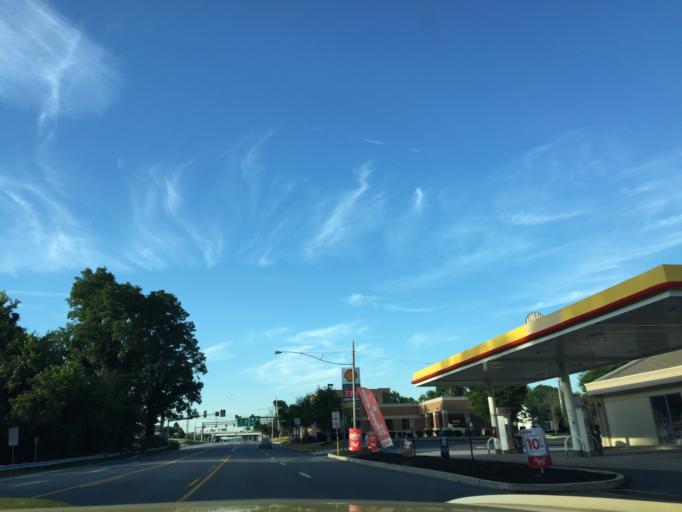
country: US
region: Pennsylvania
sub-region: Lehigh County
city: Dorneyville
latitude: 40.5722
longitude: -75.5195
